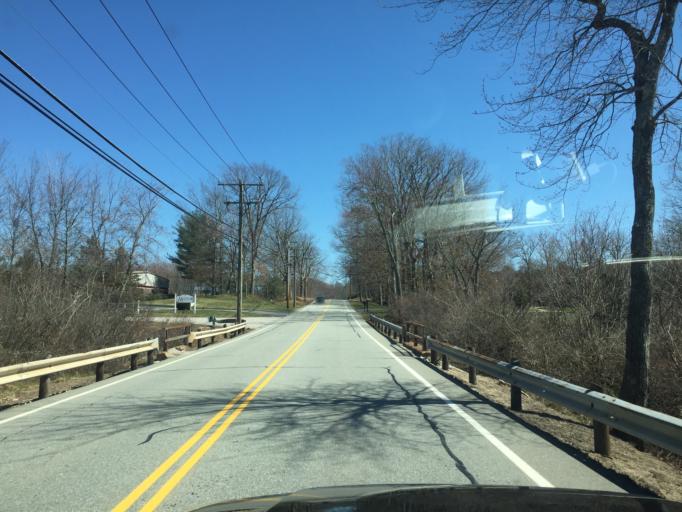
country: US
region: Connecticut
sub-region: Hartford County
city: Terramuggus
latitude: 41.6481
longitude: -72.4836
